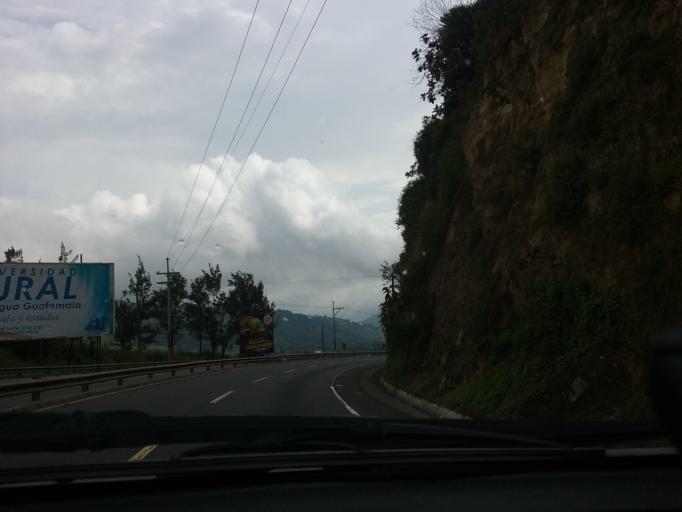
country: GT
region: Sacatepequez
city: Sumpango
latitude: 14.6382
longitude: -90.7436
